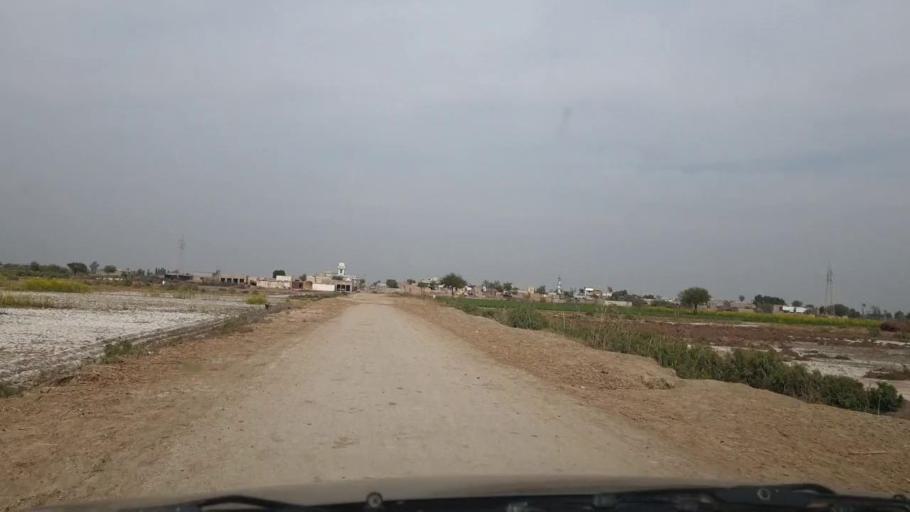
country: PK
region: Sindh
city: Sinjhoro
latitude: 26.1004
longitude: 68.8274
